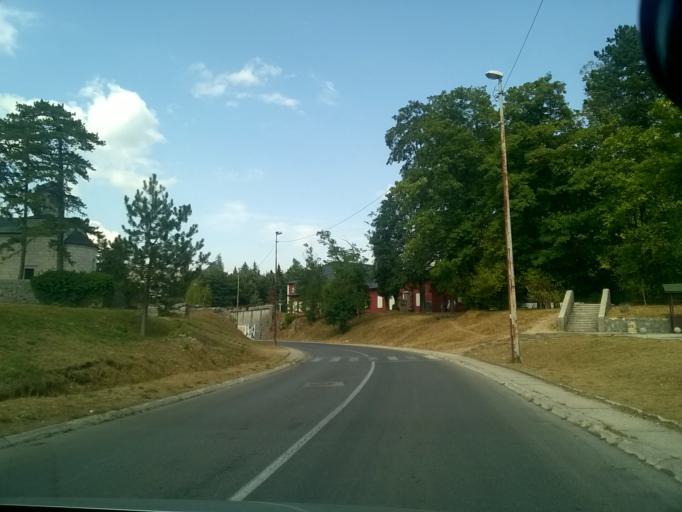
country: ME
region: Cetinje
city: Cetinje
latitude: 42.3864
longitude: 18.9237
